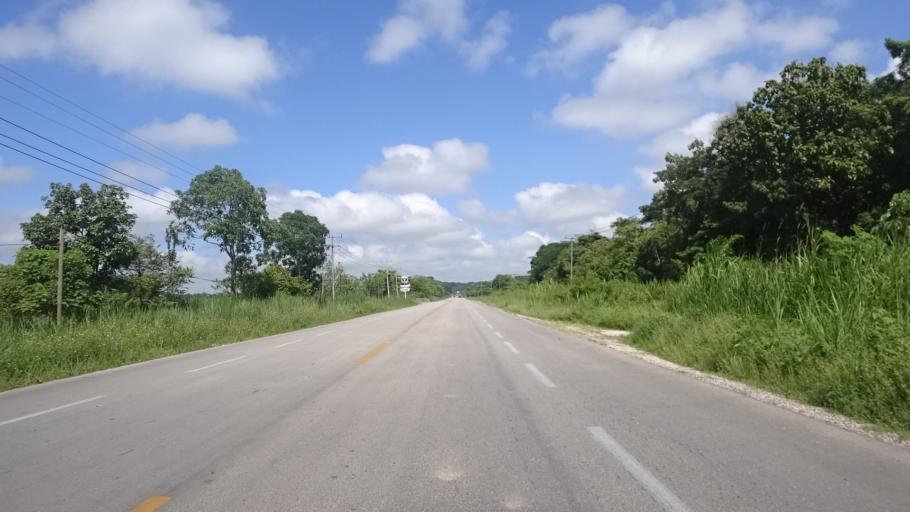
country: MX
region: Chiapas
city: Palenque
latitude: 17.4864
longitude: -91.9777
